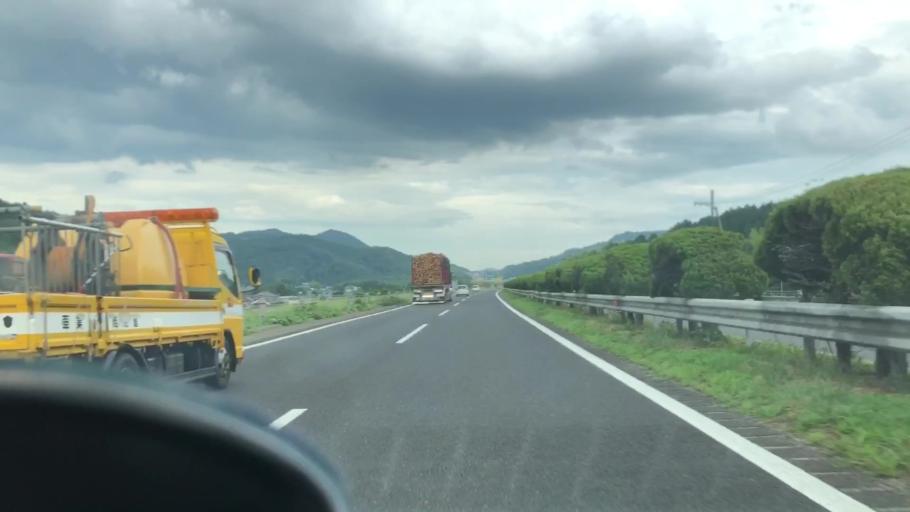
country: JP
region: Hyogo
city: Yamazakicho-nakabirose
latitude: 34.9709
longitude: 134.6660
